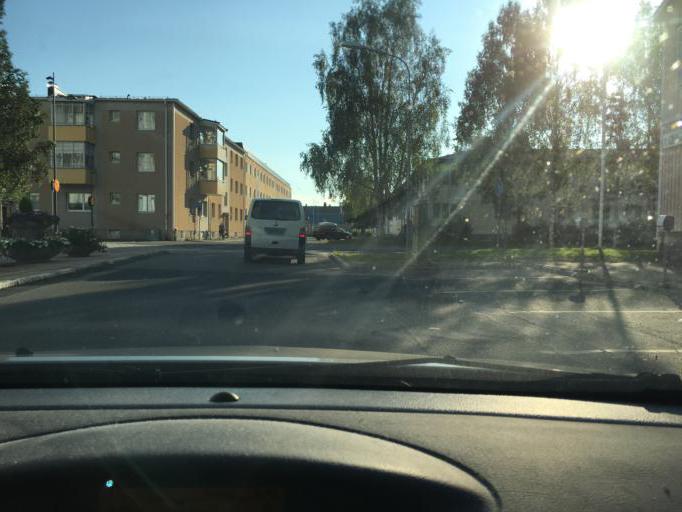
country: SE
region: Norrbotten
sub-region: Bodens Kommun
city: Boden
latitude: 65.8262
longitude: 21.6890
